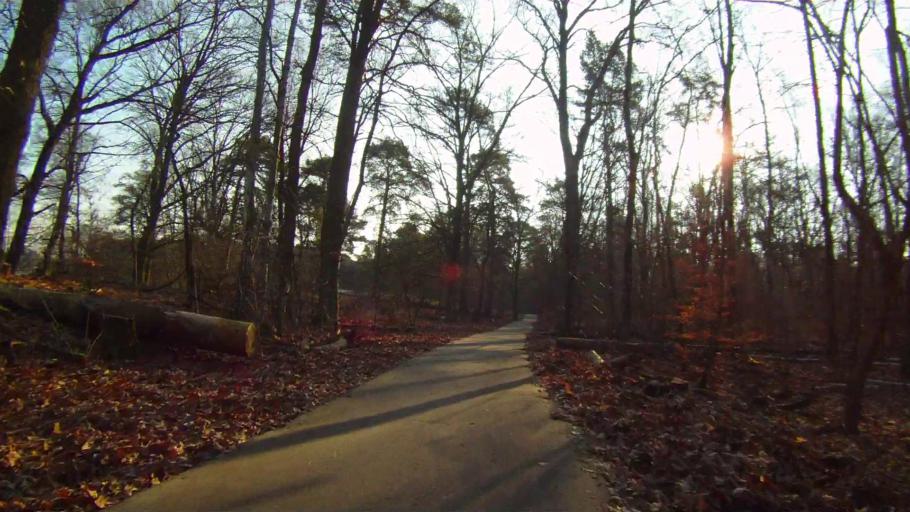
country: DE
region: Berlin
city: Rahnsdorf
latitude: 52.4284
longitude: 13.6748
